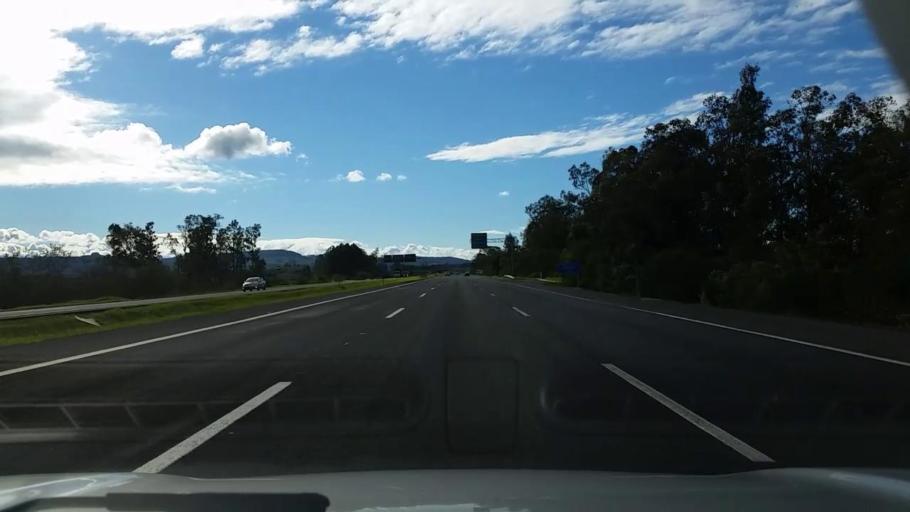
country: BR
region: Rio Grande do Sul
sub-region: Rolante
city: Rolante
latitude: -29.8814
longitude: -50.5229
